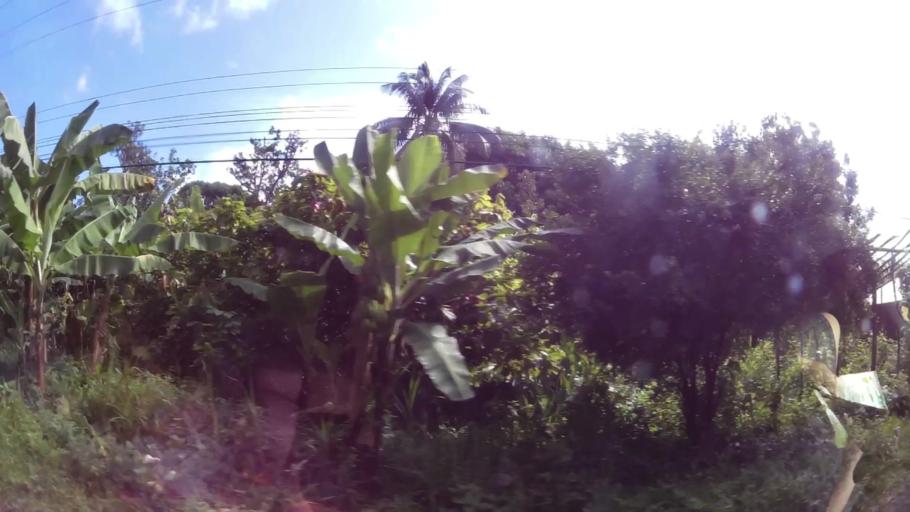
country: DM
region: Saint David
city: Castle Bruce
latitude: 15.4667
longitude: -61.2482
